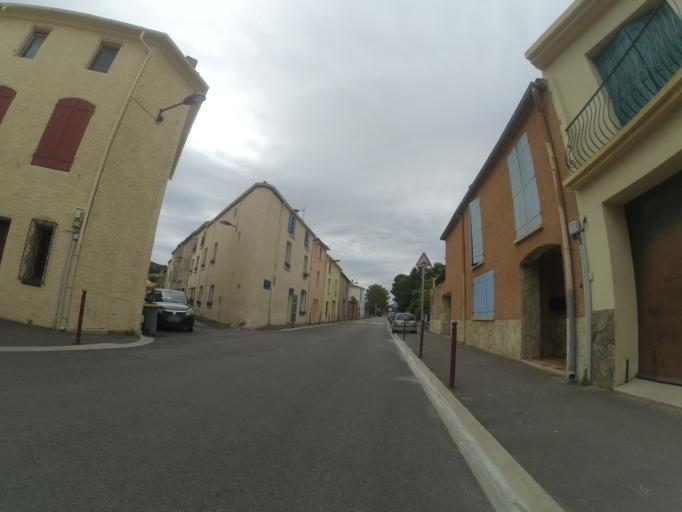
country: FR
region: Languedoc-Roussillon
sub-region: Departement des Pyrenees-Orientales
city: Estagel
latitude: 42.7713
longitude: 2.6970
